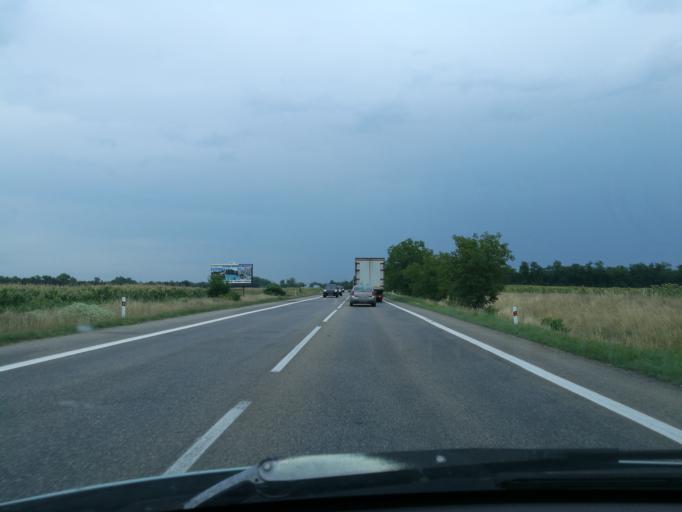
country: SK
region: Nitriansky
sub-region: Okres Nove Zamky
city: Nove Zamky
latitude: 47.9413
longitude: 18.1992
